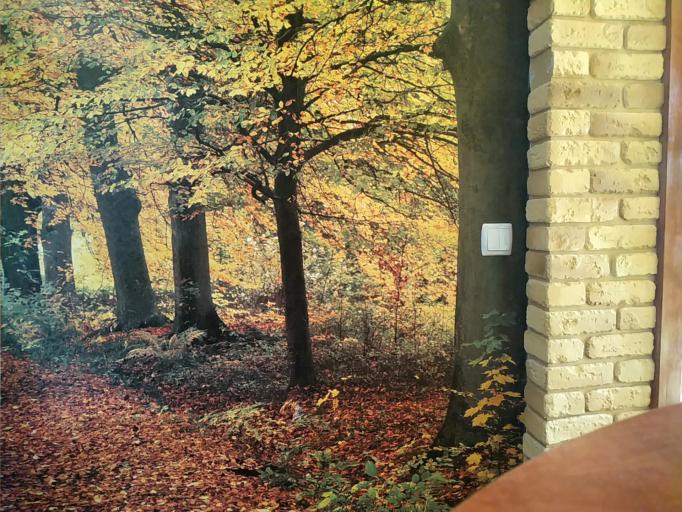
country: RU
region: Vologda
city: Molochnoye
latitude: 58.9488
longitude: 39.6511
